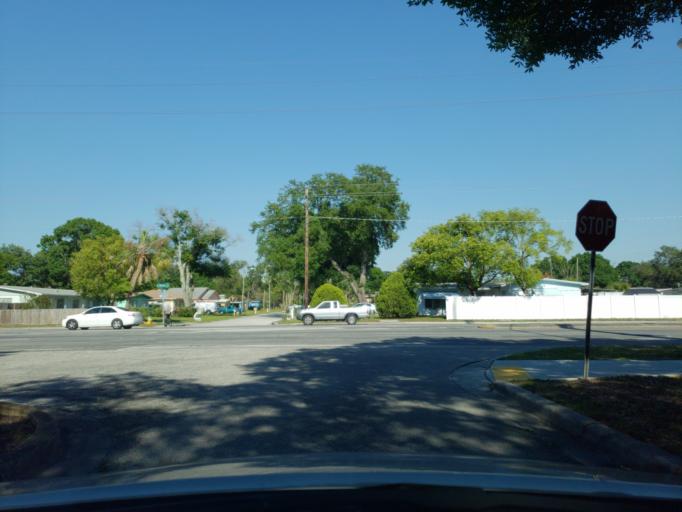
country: US
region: Florida
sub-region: Hillsborough County
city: Egypt Lake-Leto
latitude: 27.9904
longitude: -82.5015
